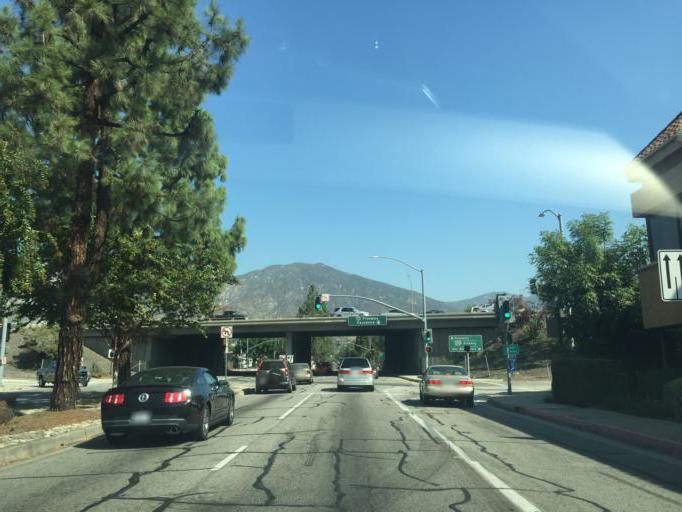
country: US
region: California
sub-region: Los Angeles County
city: Arcadia
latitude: 34.1470
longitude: -118.0315
